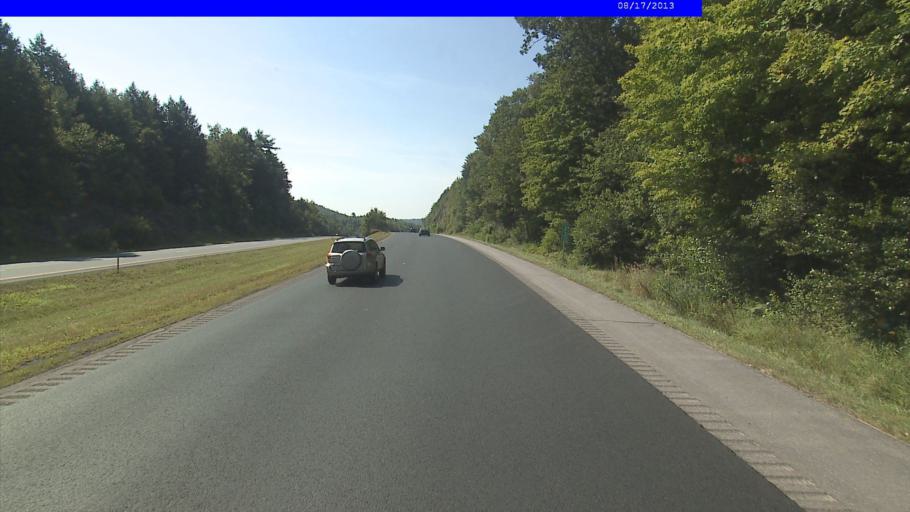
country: US
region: Vermont
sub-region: Windham County
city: Bellows Falls
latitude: 43.1502
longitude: -72.4750
